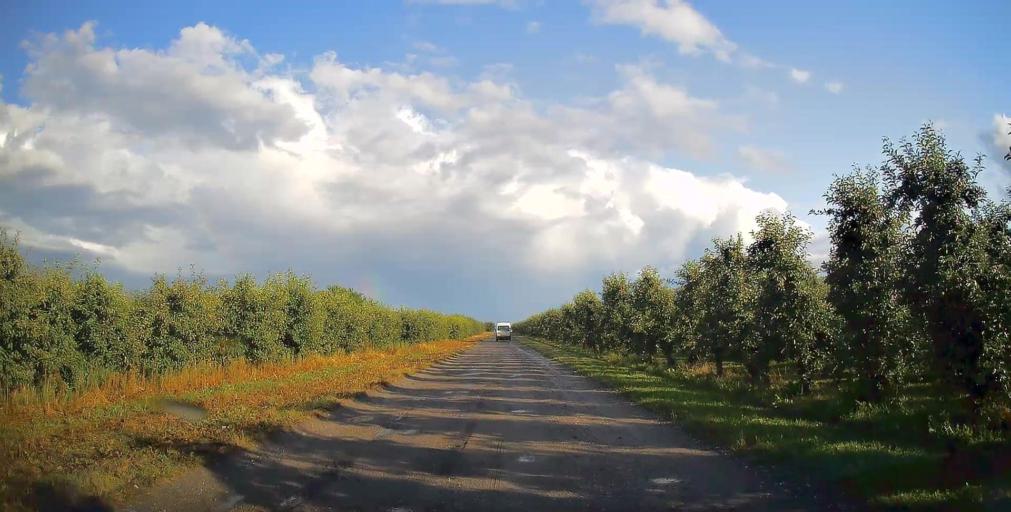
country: PL
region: Masovian Voivodeship
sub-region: Powiat grojecki
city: Goszczyn
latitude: 51.7483
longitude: 20.8861
